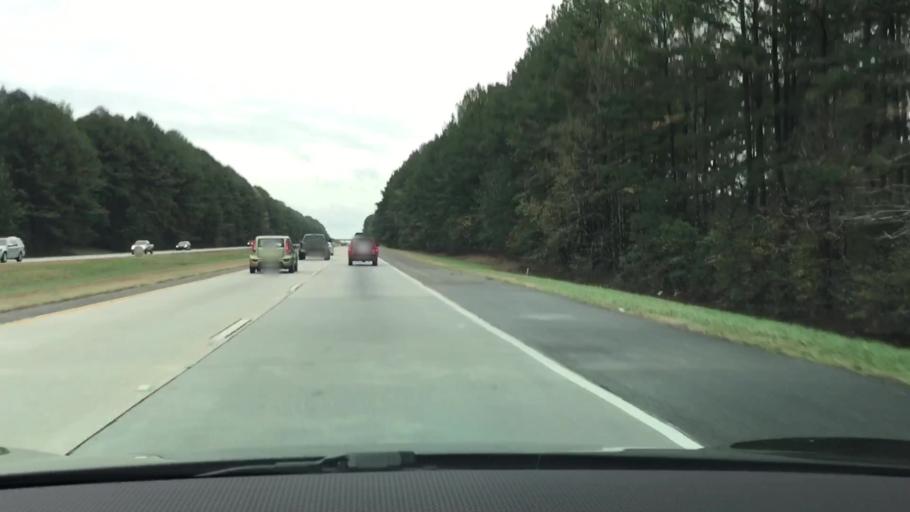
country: US
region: Georgia
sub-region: Greene County
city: Union Point
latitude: 33.5432
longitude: -83.0205
